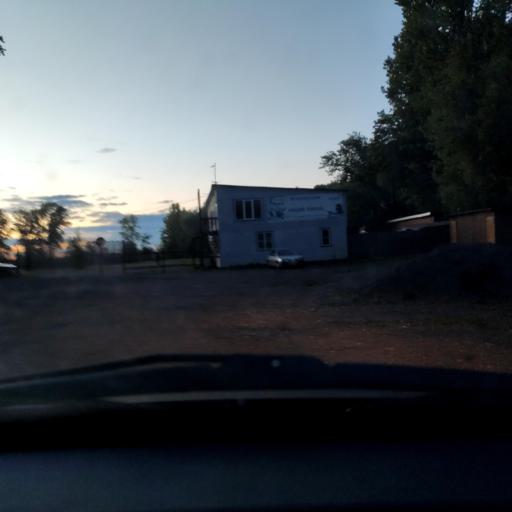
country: RU
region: Bashkortostan
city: Ufa
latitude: 54.8146
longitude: 56.0443
